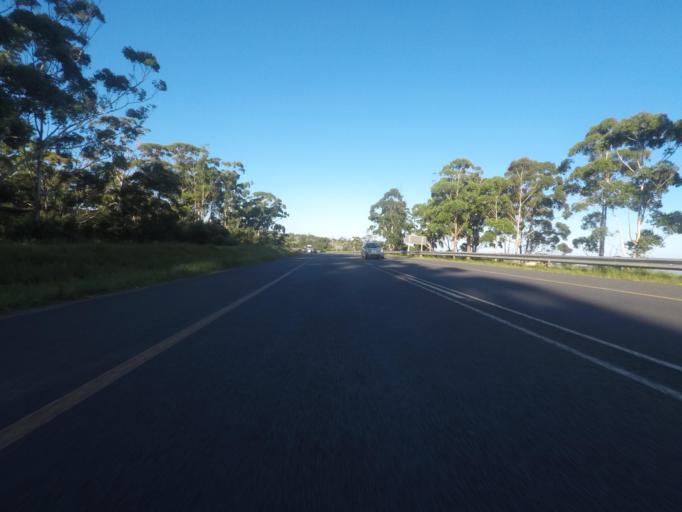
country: ZA
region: Eastern Cape
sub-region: Buffalo City Metropolitan Municipality
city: East London
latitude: -33.0453
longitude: 27.8258
